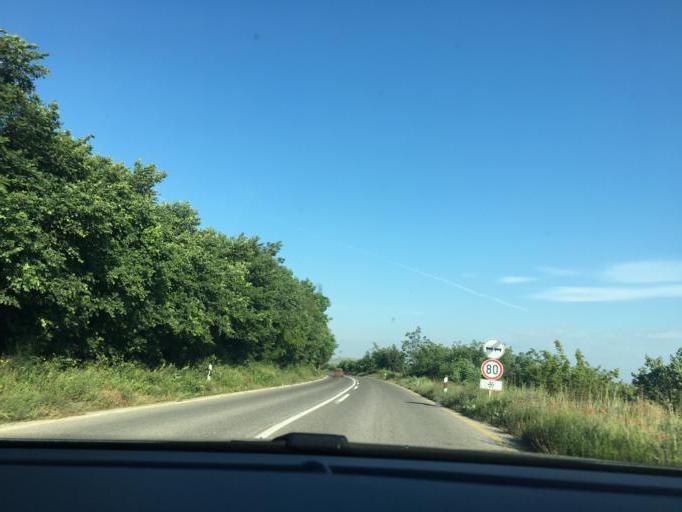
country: MK
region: Demir Kapija
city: Demir Kapija
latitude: 41.4194
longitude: 22.2269
